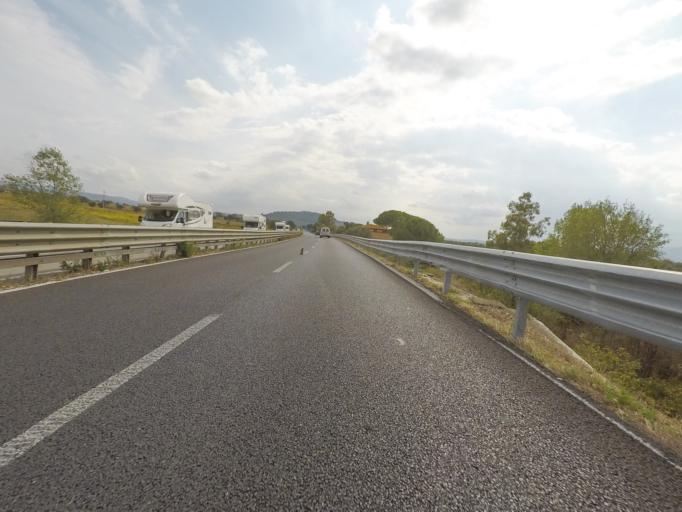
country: IT
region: Tuscany
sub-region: Provincia di Grosseto
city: Grosseto
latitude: 42.7221
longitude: 11.1384
